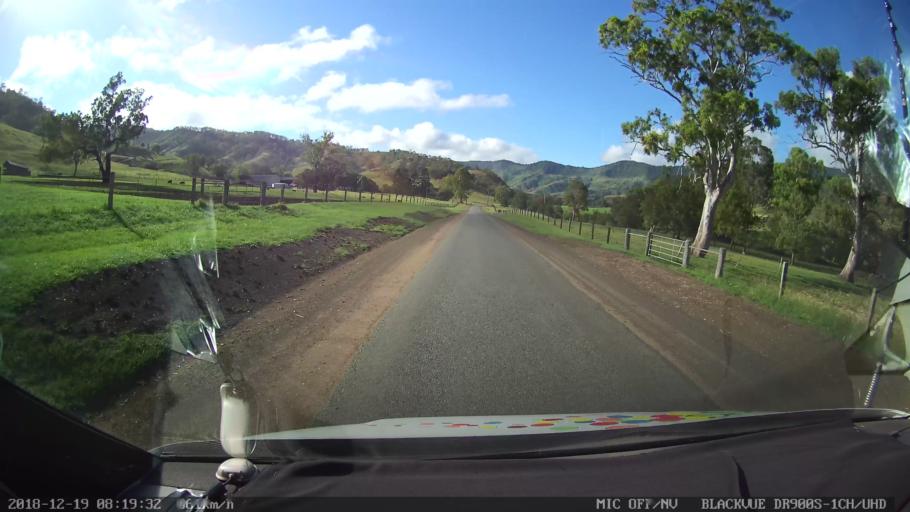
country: AU
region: New South Wales
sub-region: Kyogle
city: Kyogle
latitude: -28.2828
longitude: 152.9093
